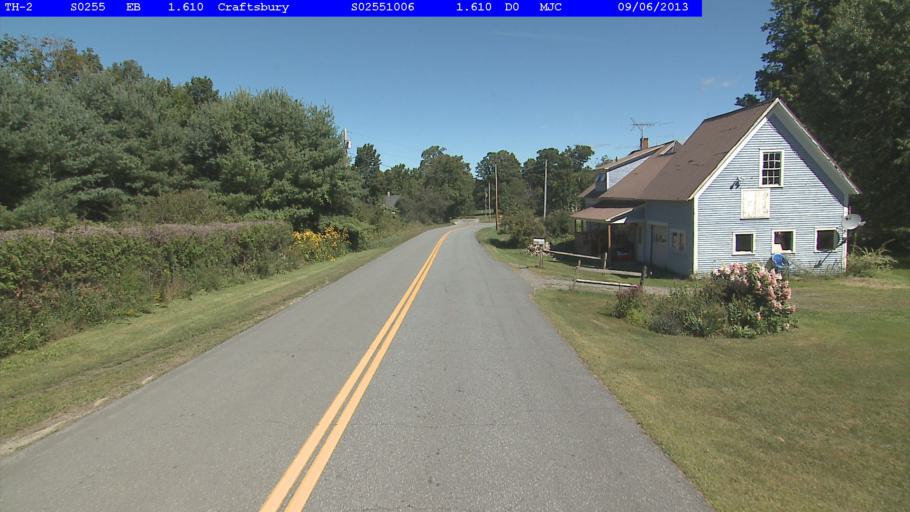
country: US
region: Vermont
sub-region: Caledonia County
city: Hardwick
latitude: 44.6402
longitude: -72.3441
